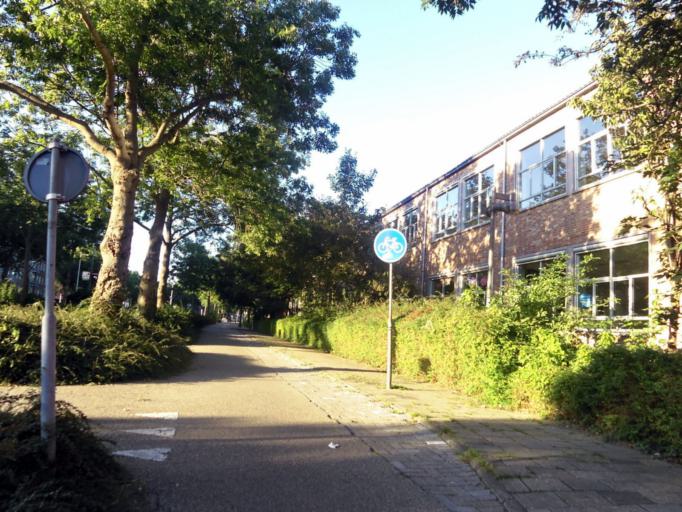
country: NL
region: South Holland
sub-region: Gemeente Alphen aan den Rijn
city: Alphen aan den Rijn
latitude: 52.1331
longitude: 4.6569
